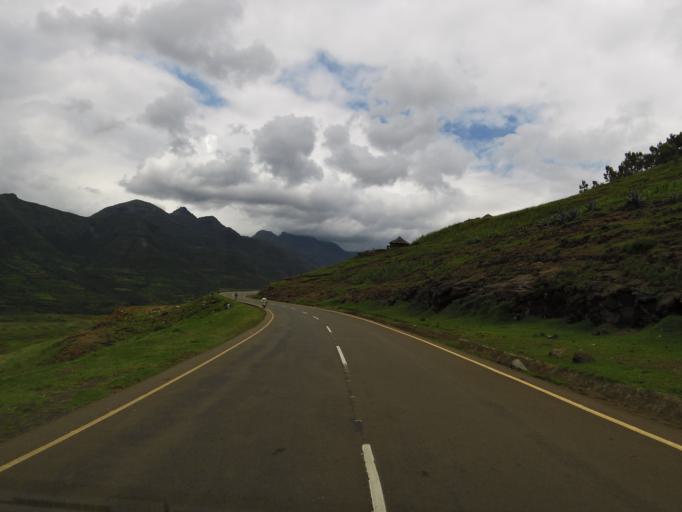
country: LS
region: Butha-Buthe
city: Butha-Buthe
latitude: -29.0362
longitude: 28.2981
